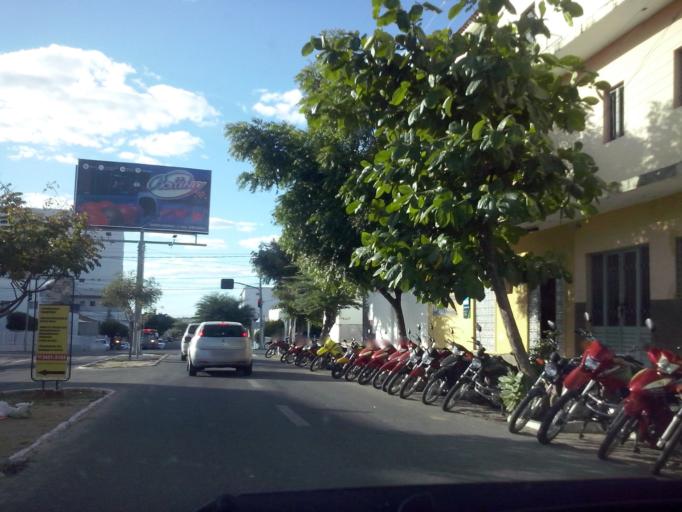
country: BR
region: Paraiba
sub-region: Patos
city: Patos
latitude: -7.0261
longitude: -37.2753
